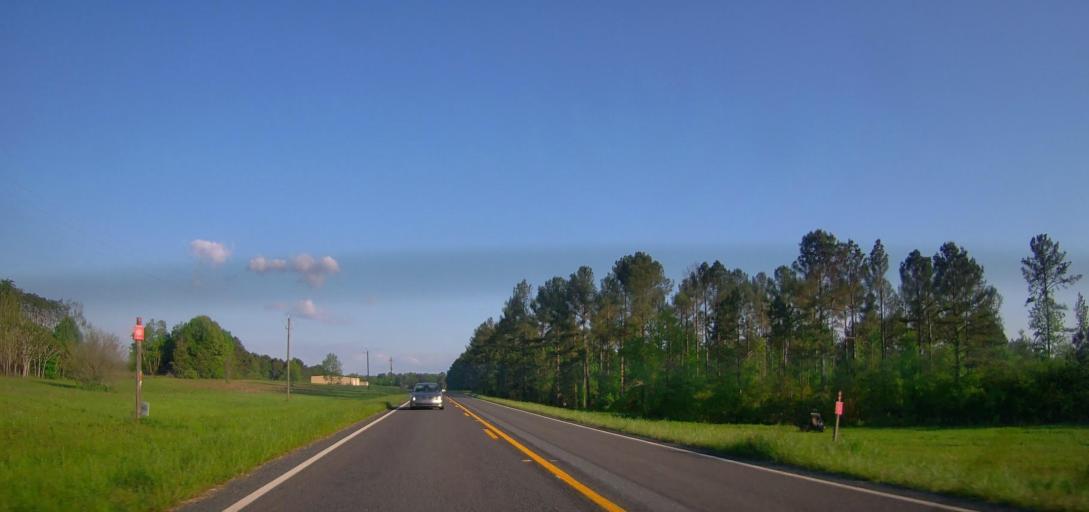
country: US
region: Georgia
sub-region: Jasper County
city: Monticello
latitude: 33.4685
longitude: -83.6384
